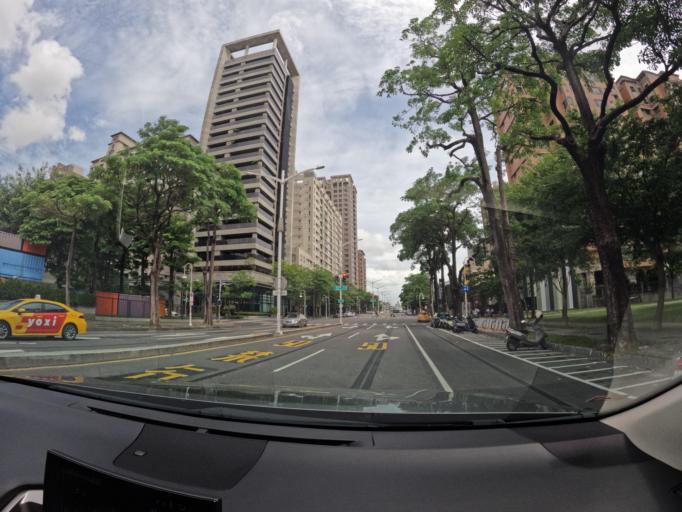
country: TW
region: Kaohsiung
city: Kaohsiung
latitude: 22.6546
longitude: 120.2881
